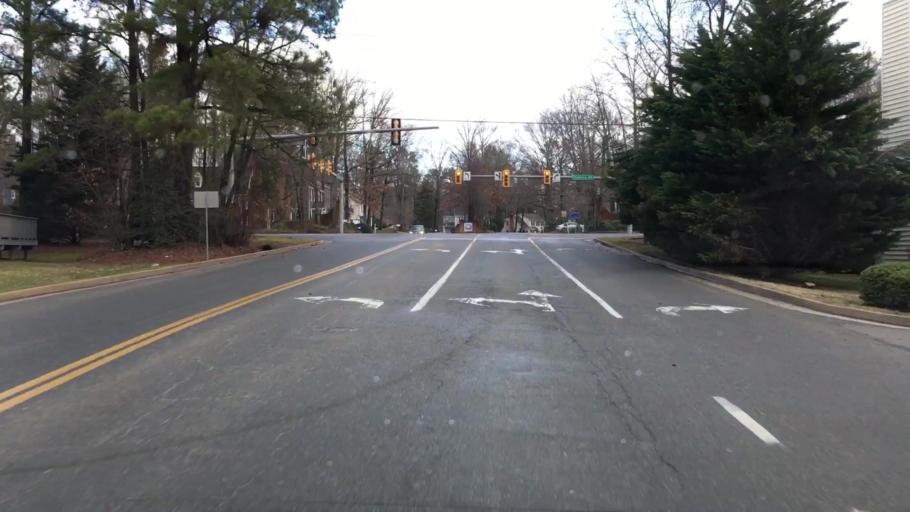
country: US
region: Virginia
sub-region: Chesterfield County
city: Bon Air
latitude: 37.5137
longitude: -77.5914
